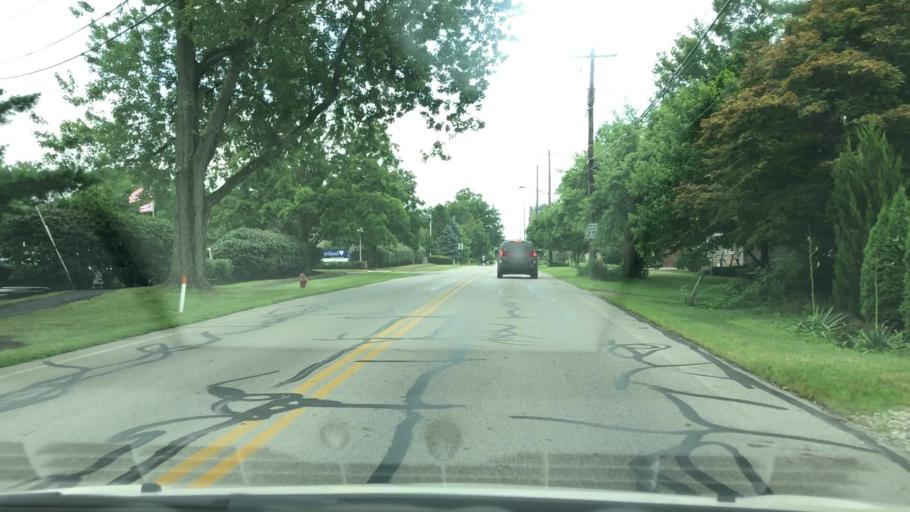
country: US
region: Ohio
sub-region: Franklin County
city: Westerville
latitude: 40.1332
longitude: -82.9280
